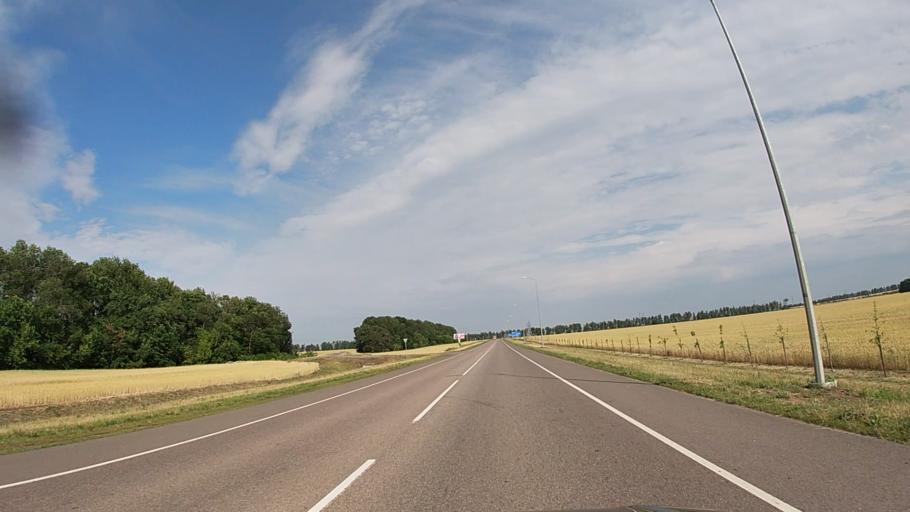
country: RU
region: Belgorod
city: Proletarskiy
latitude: 50.8280
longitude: 35.7751
